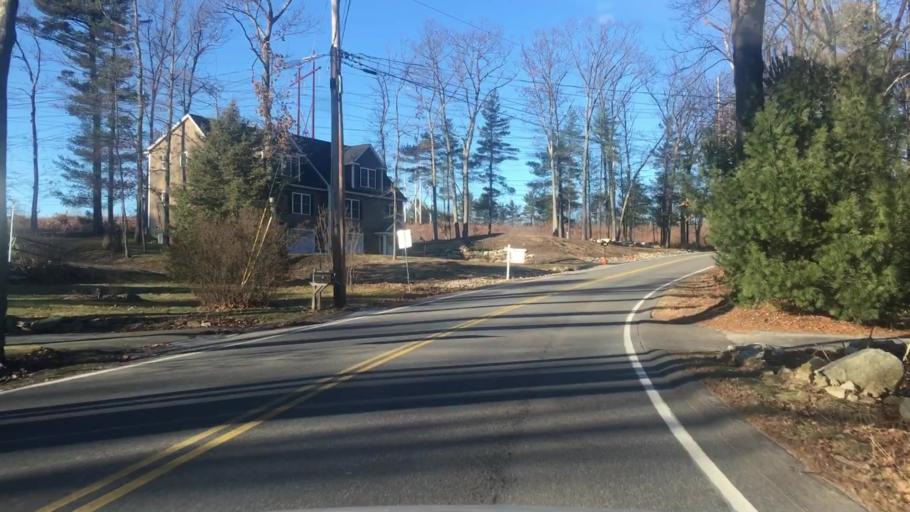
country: US
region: New Hampshire
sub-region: Rockingham County
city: Londonderry
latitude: 42.8867
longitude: -71.3704
